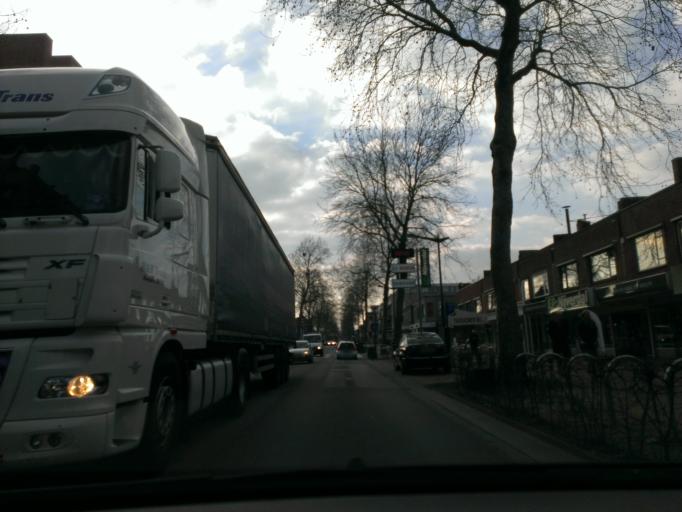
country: NL
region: Overijssel
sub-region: Gemeente Twenterand
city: Den Ham
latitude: 52.3653
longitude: 6.4622
